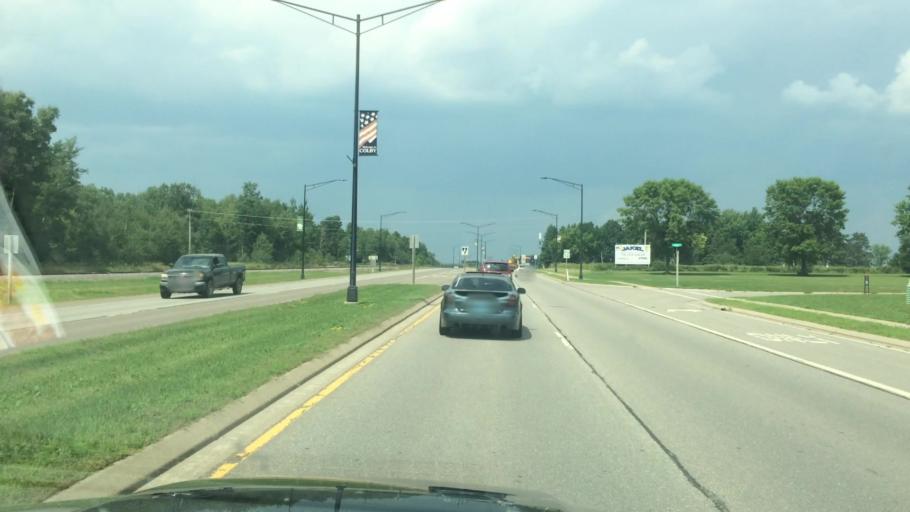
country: US
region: Wisconsin
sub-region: Clark County
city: Colby
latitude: 44.9219
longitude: -90.3151
